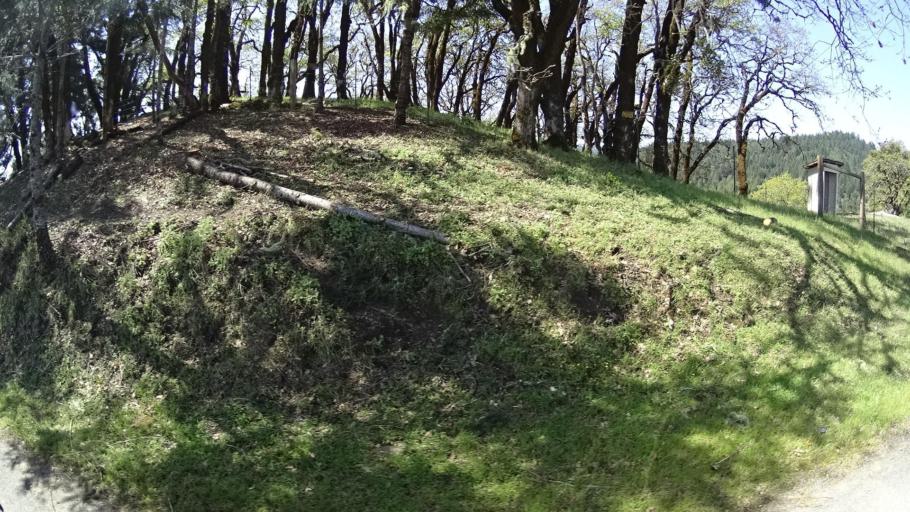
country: US
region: California
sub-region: Humboldt County
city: Redway
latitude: 40.0309
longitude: -123.6376
